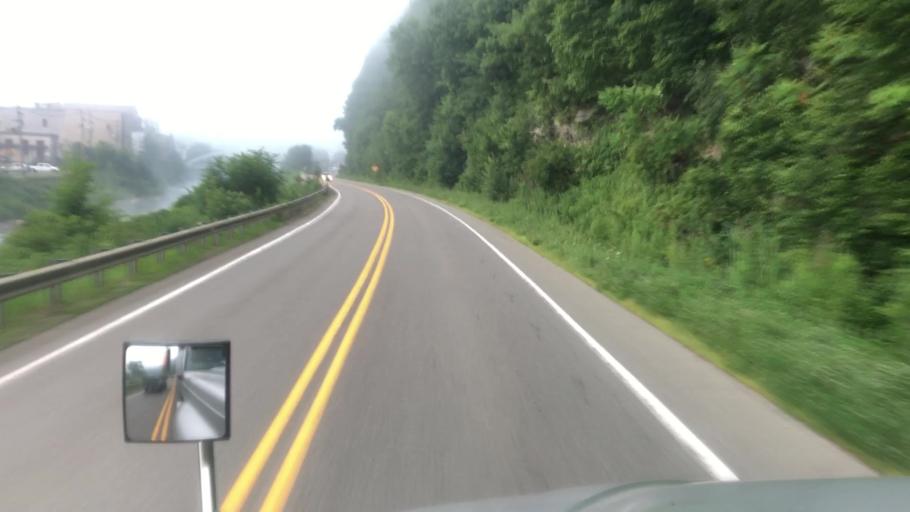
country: US
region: Pennsylvania
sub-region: Venango County
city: Oil City
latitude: 41.4379
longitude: -79.7107
